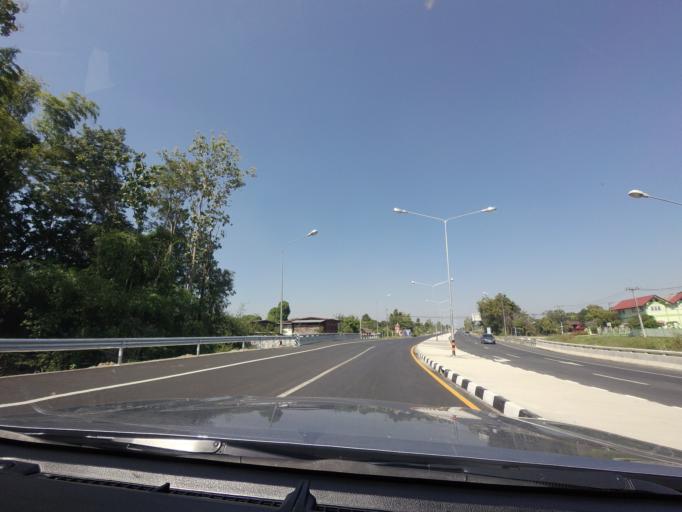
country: TH
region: Sukhothai
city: Ban Na
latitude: 17.0175
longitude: 99.7338
